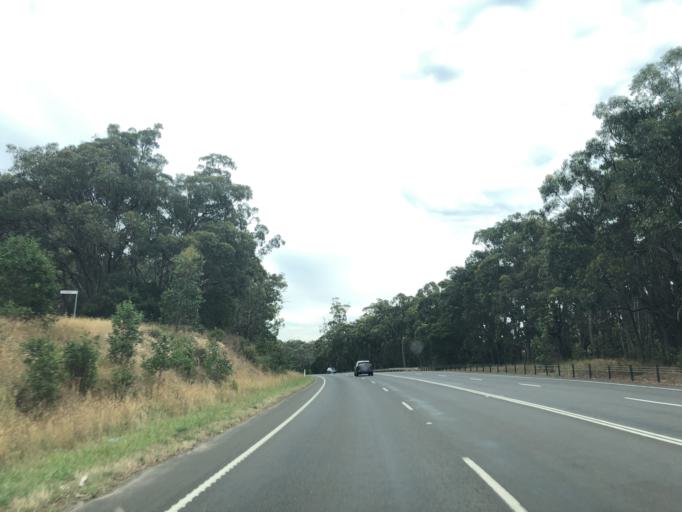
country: AU
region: Victoria
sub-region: Hume
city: Sunbury
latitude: -37.3844
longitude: 144.5265
